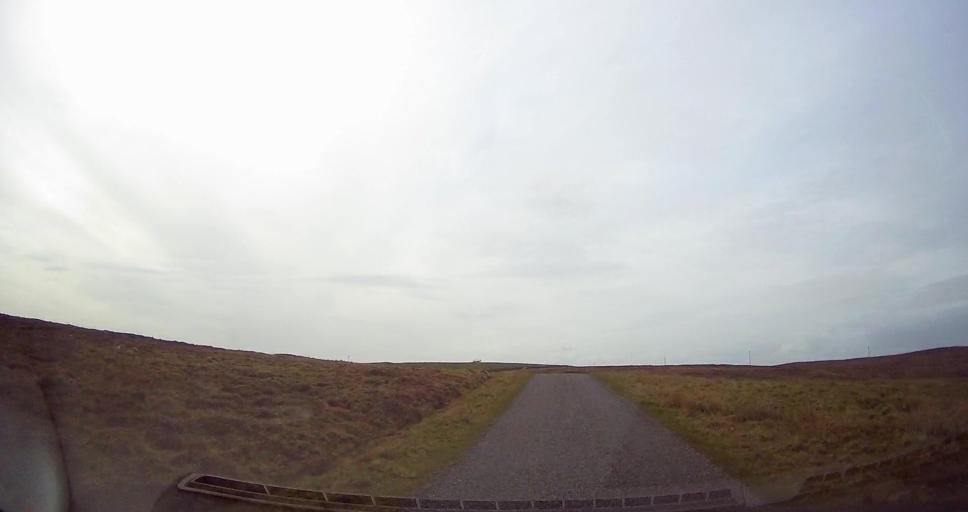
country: GB
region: Scotland
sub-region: Shetland Islands
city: Shetland
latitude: 60.1526
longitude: -1.0916
